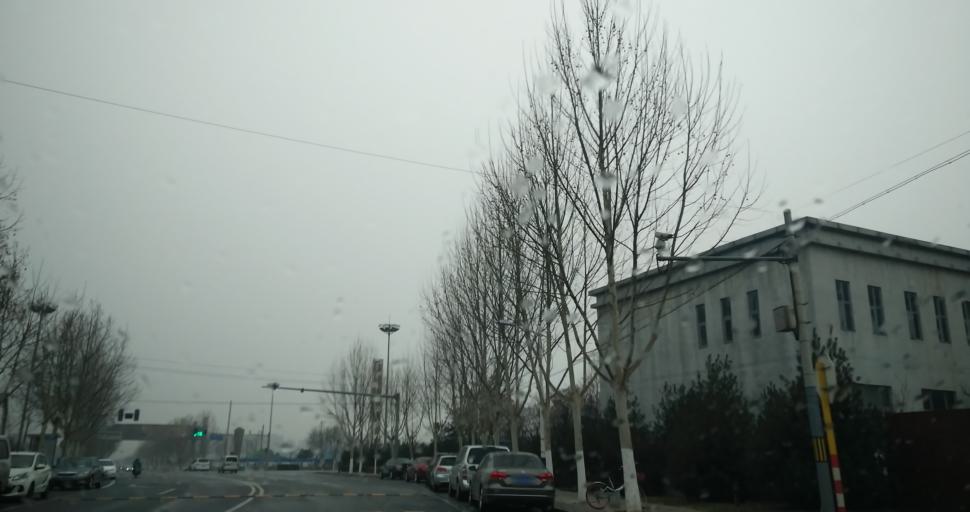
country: CN
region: Beijing
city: Yinghai
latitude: 39.7547
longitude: 116.4461
